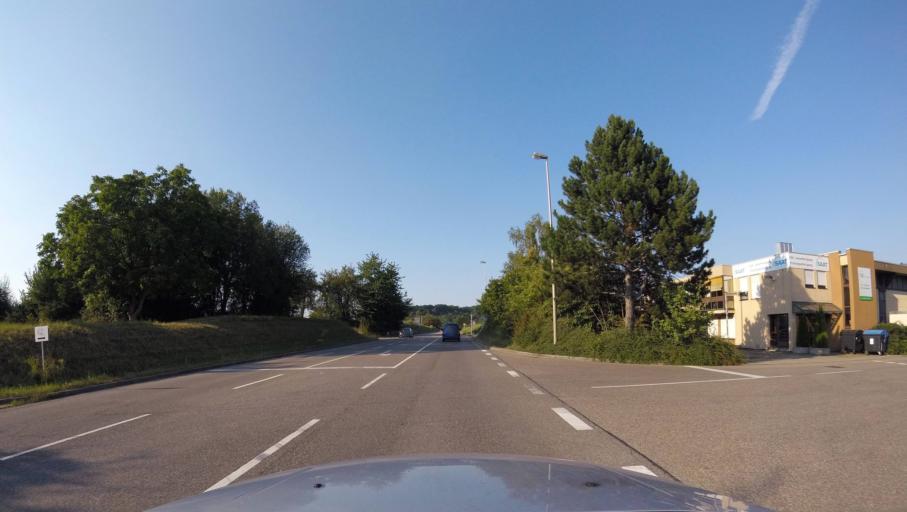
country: DE
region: Baden-Wuerttemberg
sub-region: Regierungsbezirk Stuttgart
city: Winnenden
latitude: 48.8930
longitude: 9.4235
